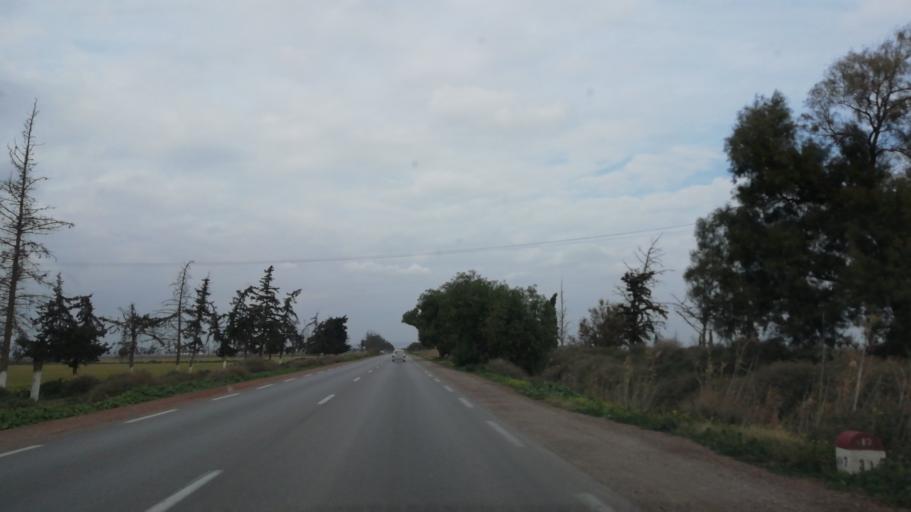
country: DZ
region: Mostaganem
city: Mostaganem
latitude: 35.6716
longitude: 0.0577
